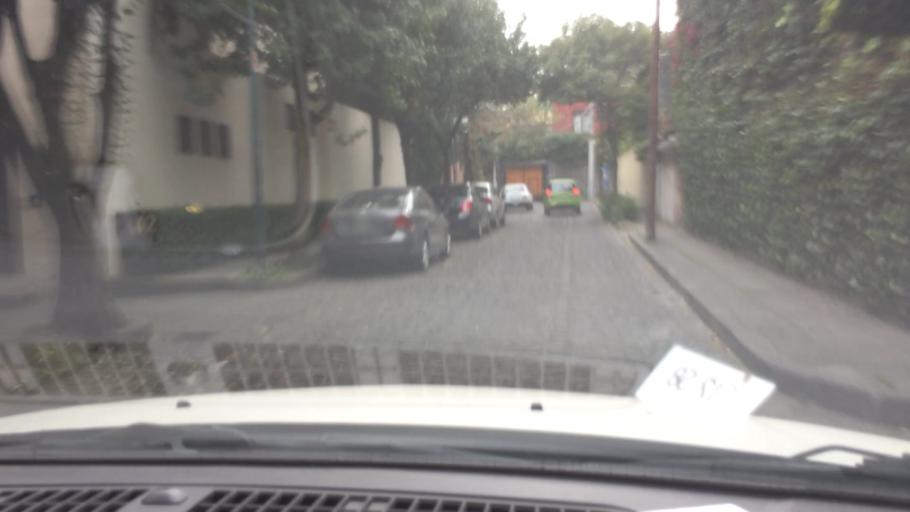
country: MX
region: Mexico City
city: Alvaro Obregon
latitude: 19.3524
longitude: -99.1926
